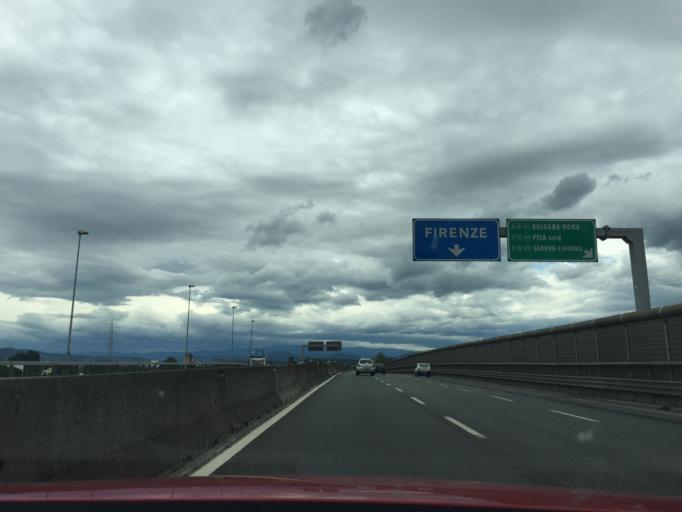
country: IT
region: Tuscany
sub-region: Province of Florence
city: Mantignano-Ugnano
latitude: 43.7731
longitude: 11.1614
